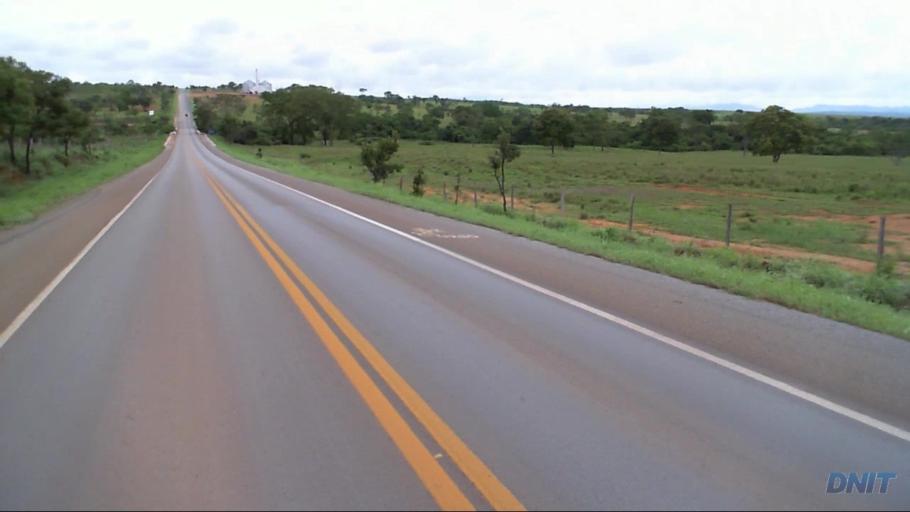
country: BR
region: Goias
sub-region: Padre Bernardo
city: Padre Bernardo
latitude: -15.1584
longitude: -48.3172
